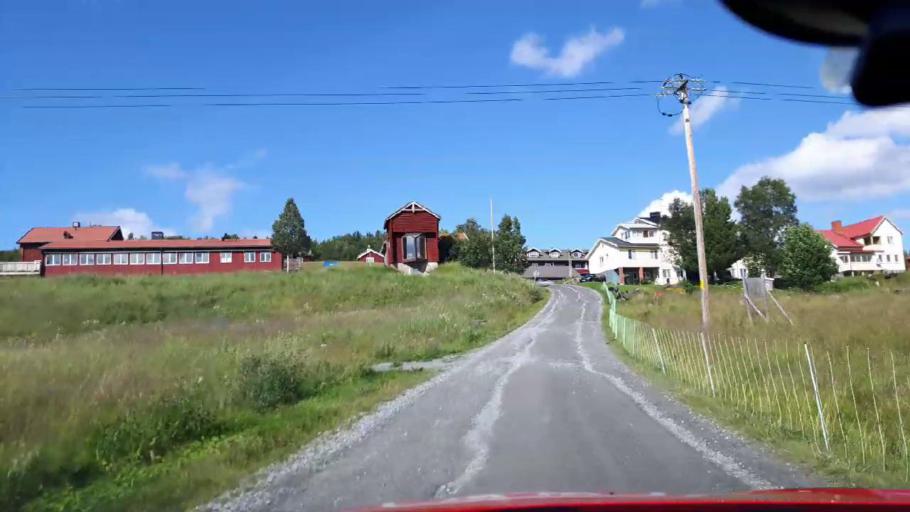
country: SE
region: Jaemtland
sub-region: Are Kommun
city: Are
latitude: 63.2146
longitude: 13.0547
